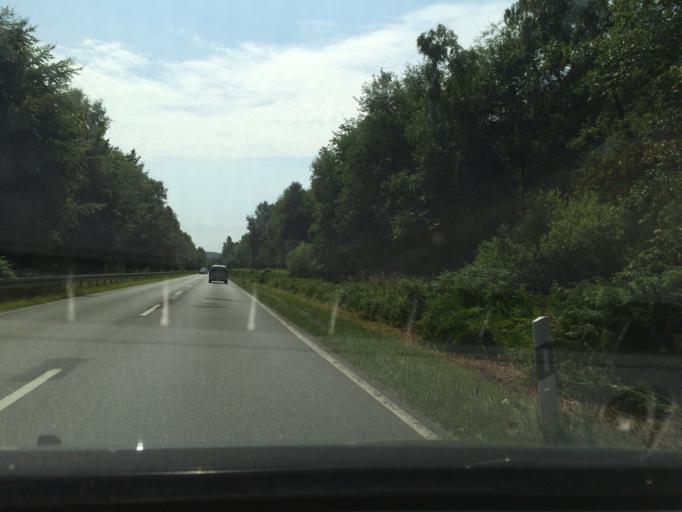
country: DE
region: Mecklenburg-Vorpommern
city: Ostseebad Binz
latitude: 54.4130
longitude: 13.5915
